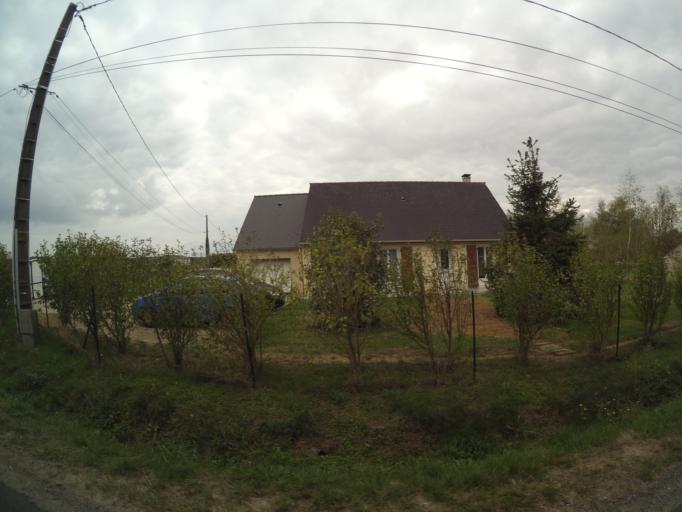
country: FR
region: Centre
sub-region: Departement d'Indre-et-Loire
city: Auzouer-en-Touraine
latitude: 47.5150
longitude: 0.9452
